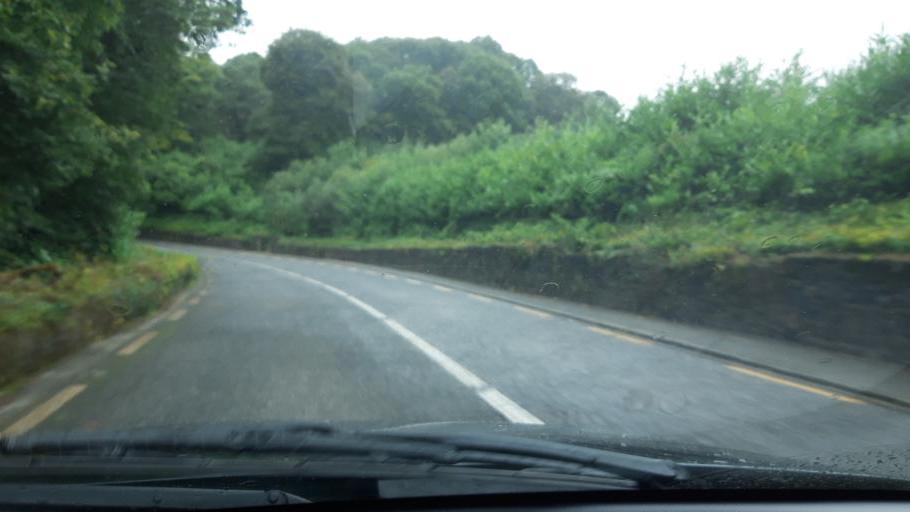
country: IE
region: Munster
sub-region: County Cork
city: Youghal
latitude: 52.1457
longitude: -7.9169
